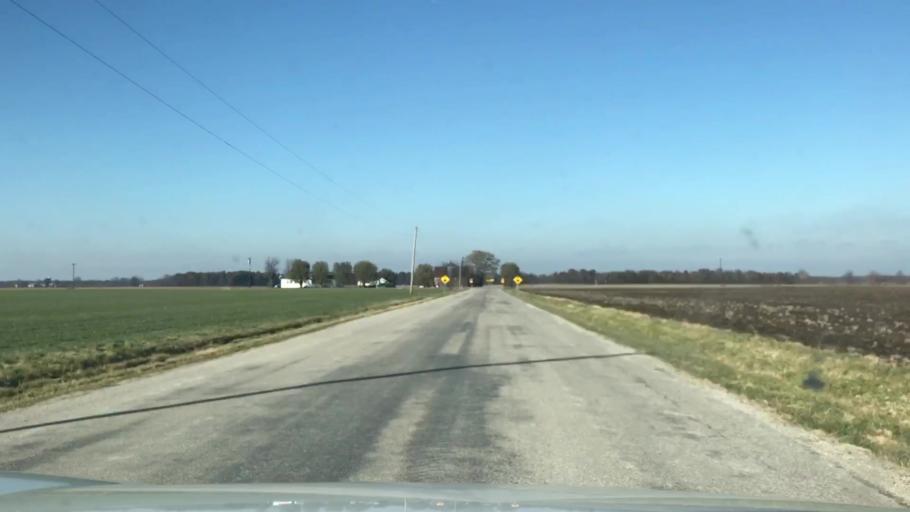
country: US
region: Illinois
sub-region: Washington County
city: Okawville
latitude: 38.4392
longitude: -89.4780
